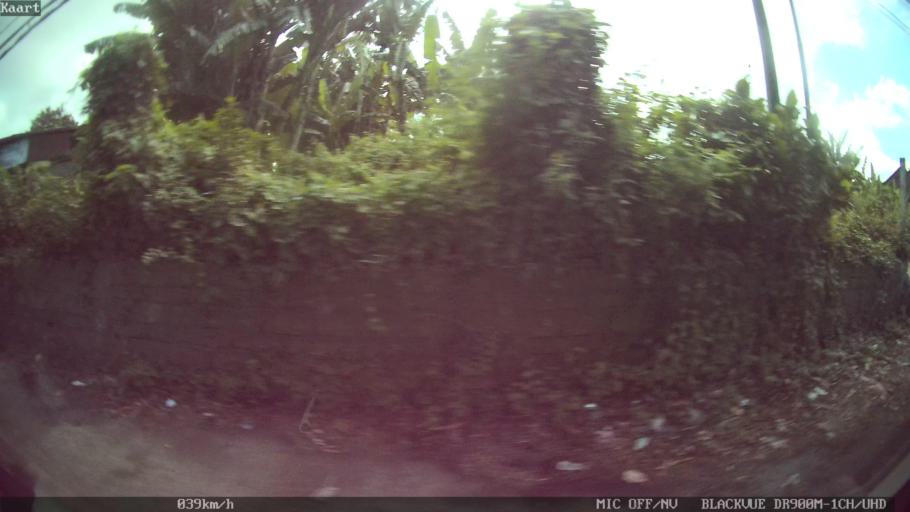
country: ID
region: Bali
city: Banjar Pasekan
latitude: -8.5993
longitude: 115.2909
